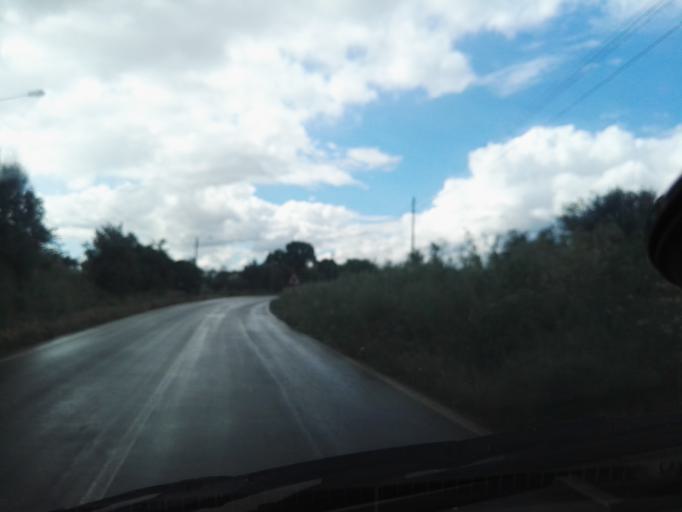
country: PT
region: Santarem
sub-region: Golega
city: Golega
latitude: 39.4137
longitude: -8.4926
